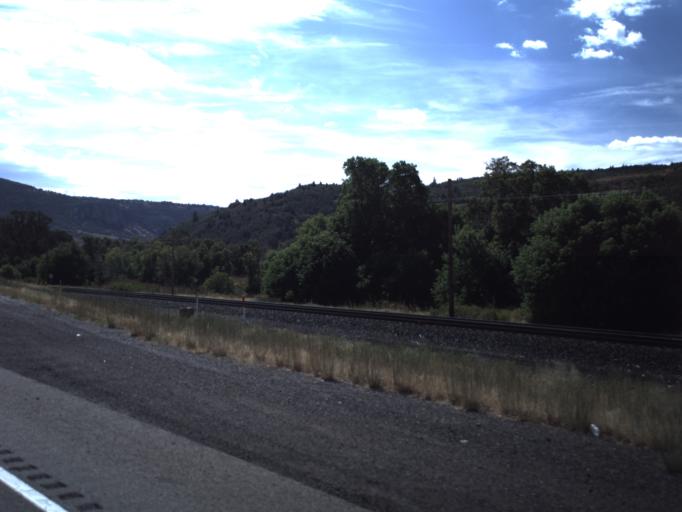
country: US
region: Utah
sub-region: Utah County
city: Mapleton
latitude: 40.0345
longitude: -111.5224
